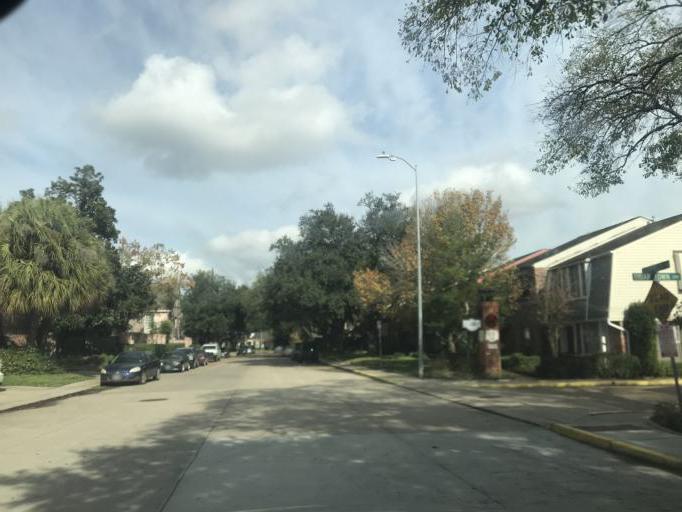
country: US
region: Texas
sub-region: Harris County
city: Hunters Creek Village
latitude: 29.7396
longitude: -95.4916
